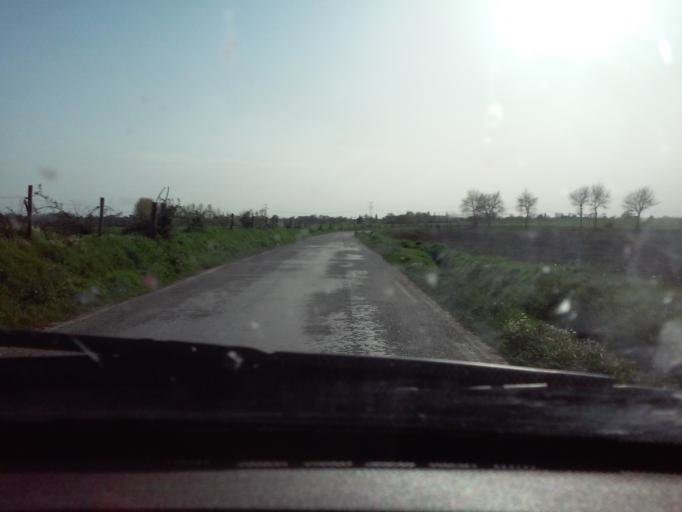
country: FR
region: Brittany
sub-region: Departement d'Ille-et-Vilaine
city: Romagne
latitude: 48.3018
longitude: -1.2719
